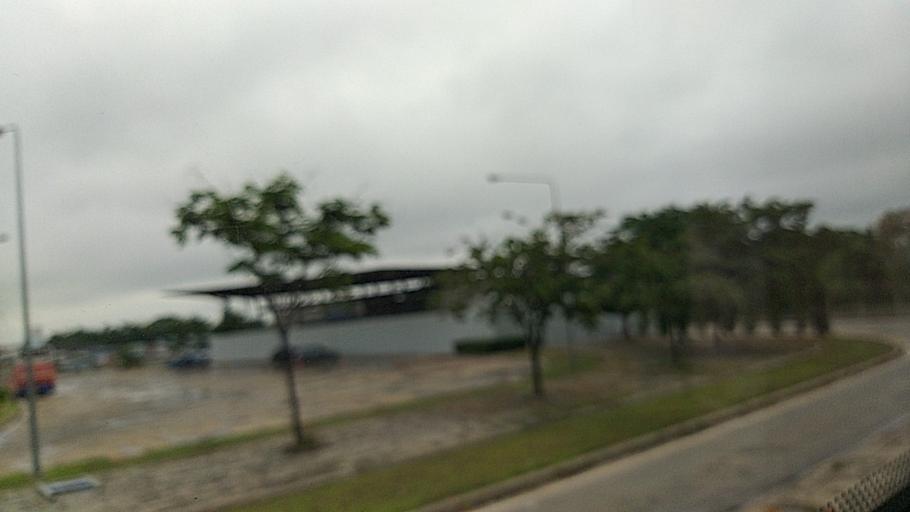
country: TH
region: Nakhon Ratchasima
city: Nakhon Ratchasima
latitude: 14.9916
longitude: 102.0925
